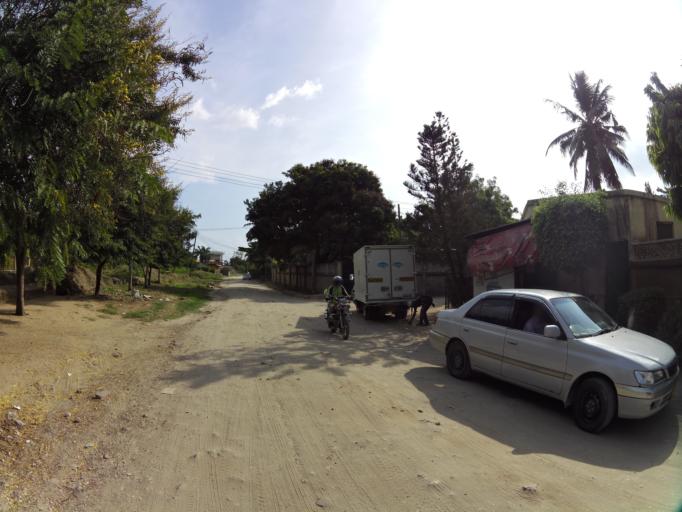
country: TZ
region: Dar es Salaam
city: Magomeni
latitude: -6.7691
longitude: 39.2493
